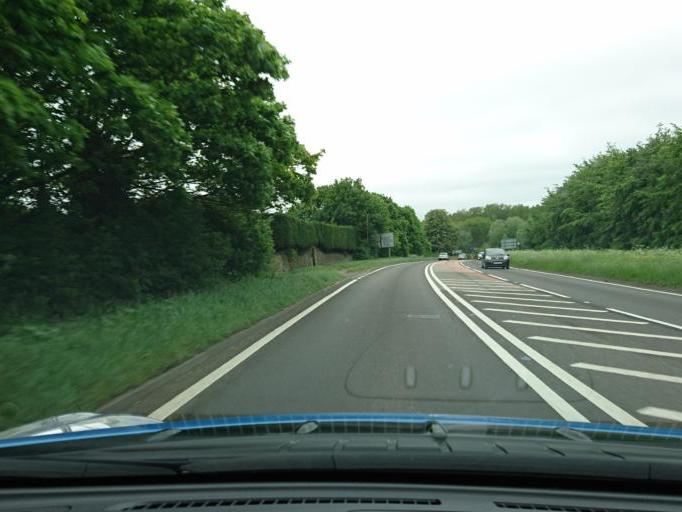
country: GB
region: England
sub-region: Oxfordshire
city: Marcham
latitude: 51.7111
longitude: -1.3371
